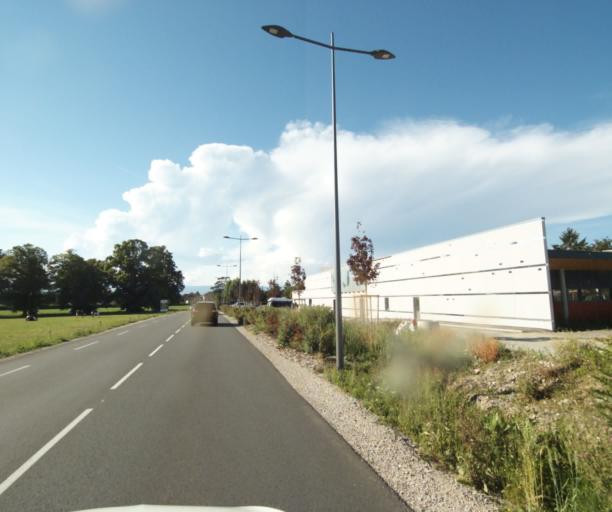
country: FR
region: Rhone-Alpes
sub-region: Departement de la Haute-Savoie
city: Douvaine
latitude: 46.3023
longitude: 6.3032
